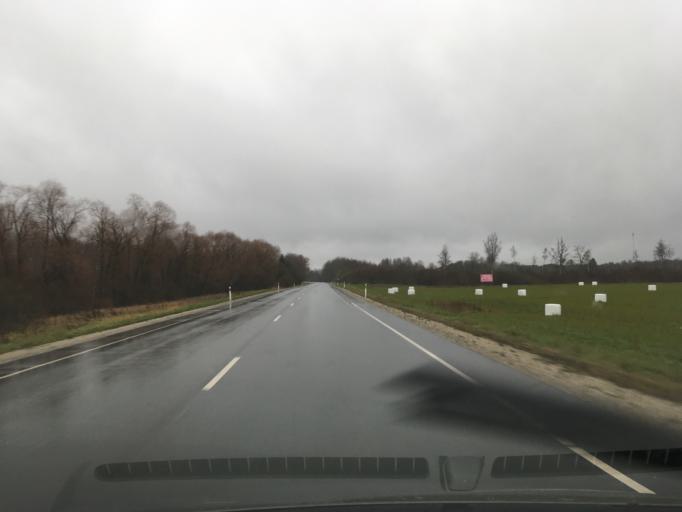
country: EE
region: Laeaene
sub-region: Lihula vald
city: Lihula
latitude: 58.8473
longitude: 24.0651
